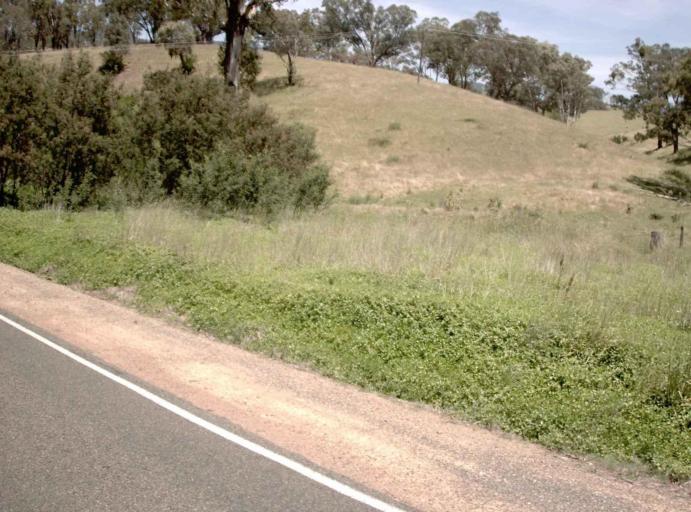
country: AU
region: Victoria
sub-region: East Gippsland
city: Bairnsdale
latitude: -37.3937
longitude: 147.8347
